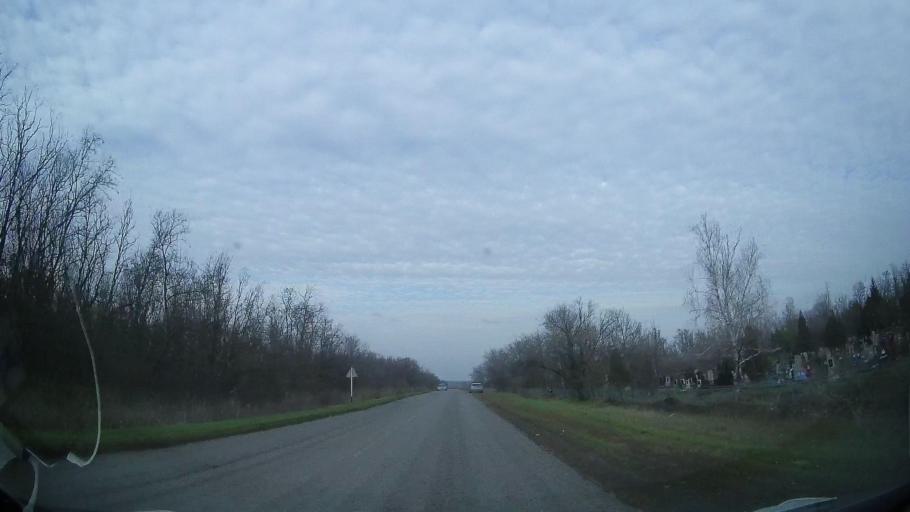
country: RU
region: Rostov
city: Zernograd
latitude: 46.8757
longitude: 40.3348
